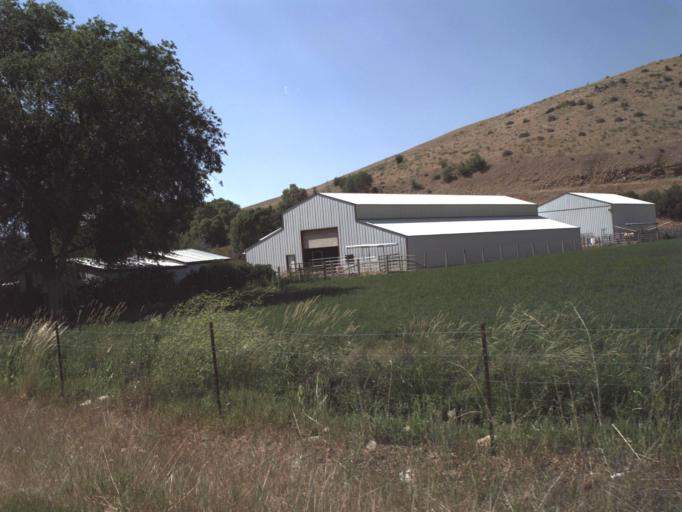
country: US
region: Utah
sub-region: Weber County
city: Wolf Creek
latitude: 41.2609
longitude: -111.7167
